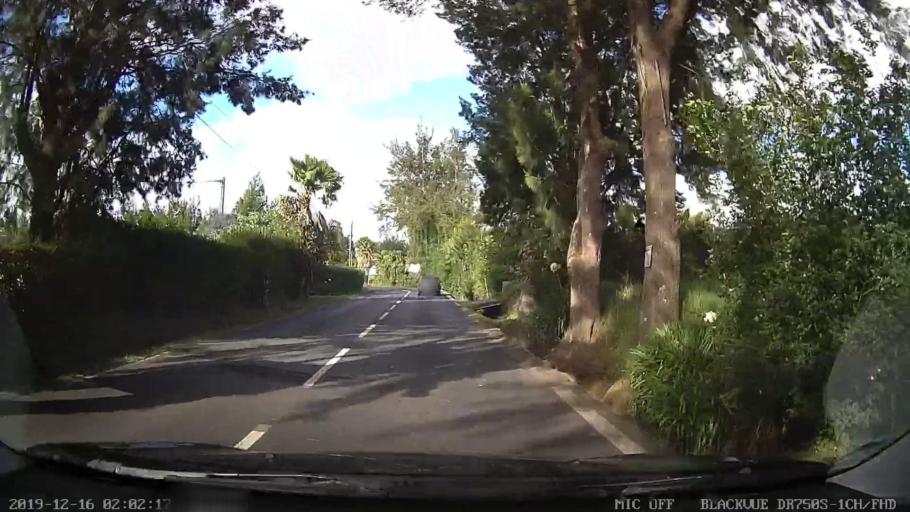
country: RE
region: Reunion
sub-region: Reunion
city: Le Tampon
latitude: -21.2185
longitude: 55.5606
